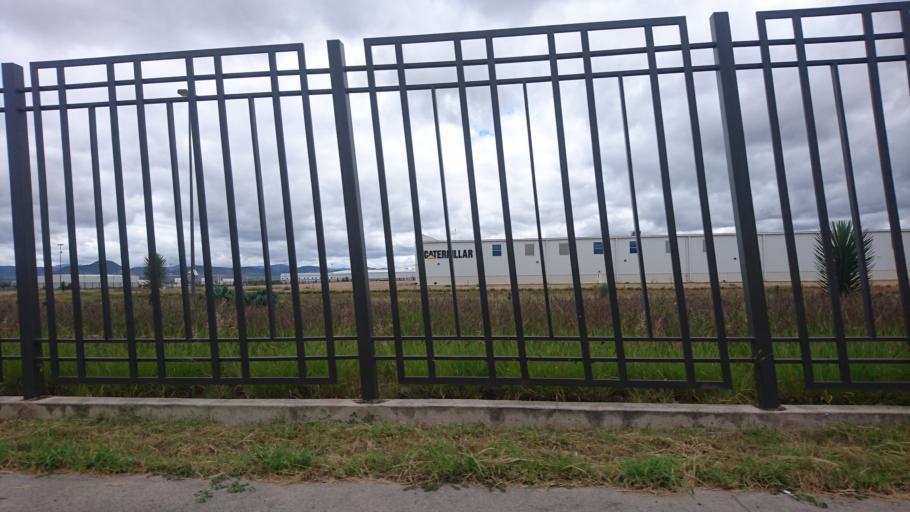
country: MX
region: San Luis Potosi
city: La Pila
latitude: 21.9856
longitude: -100.8676
